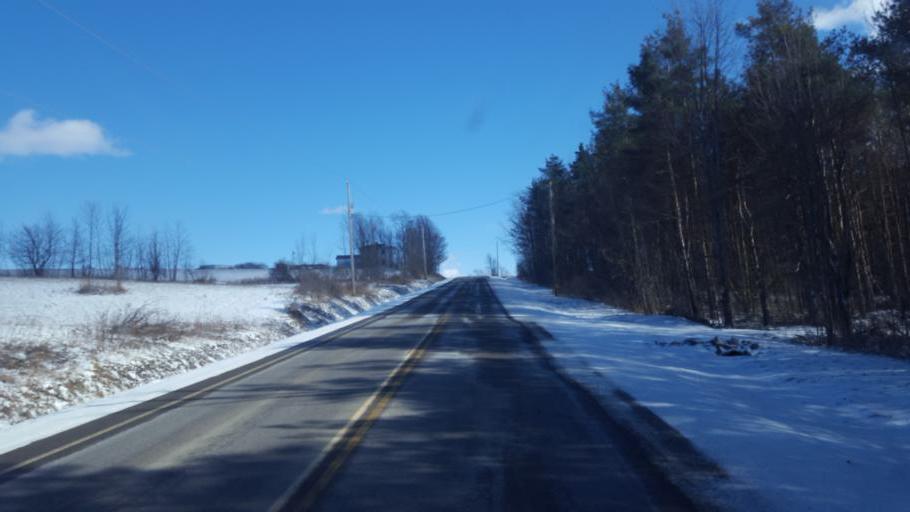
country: US
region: New York
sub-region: Allegany County
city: Friendship
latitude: 42.1965
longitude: -78.1002
